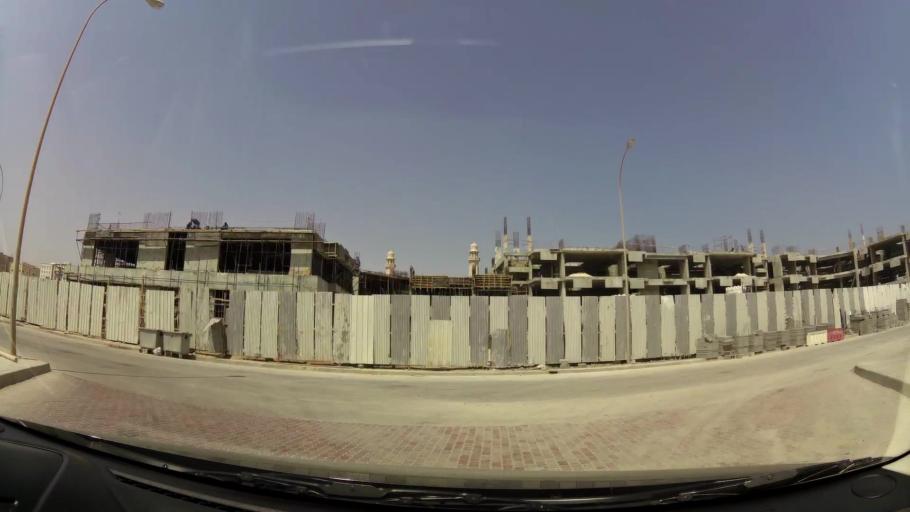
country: OM
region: Zufar
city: Salalah
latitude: 17.0168
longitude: 54.0914
